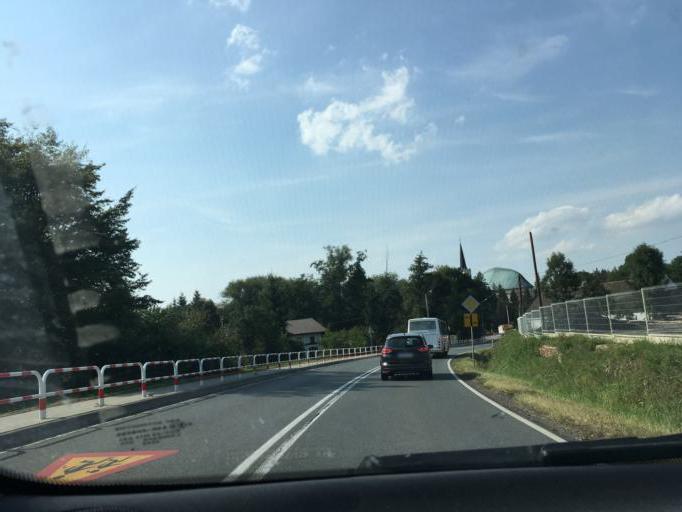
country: PL
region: Opole Voivodeship
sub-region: Powiat prudnicki
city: Laka Prudnicka
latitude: 50.3812
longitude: 17.5270
